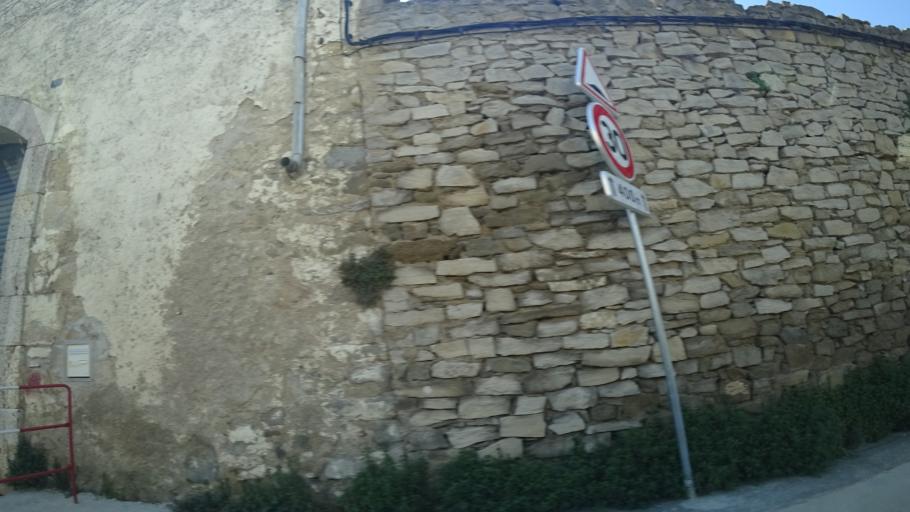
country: FR
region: Languedoc-Roussillon
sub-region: Departement de l'Herault
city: Olonzac
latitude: 43.3261
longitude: 2.7389
